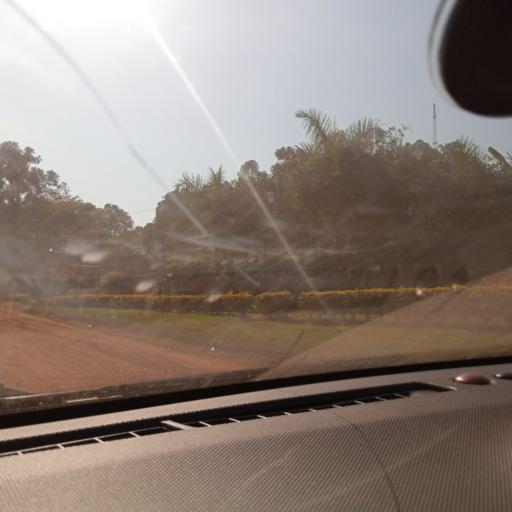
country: UG
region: Central Region
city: Masaka
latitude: -0.3362
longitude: 31.7315
